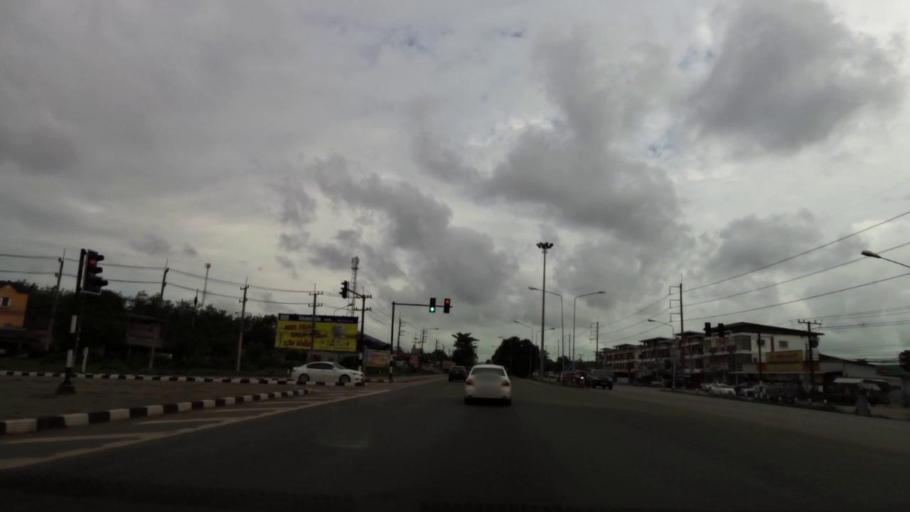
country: TH
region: Chanthaburi
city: Tha Mai
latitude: 12.7246
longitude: 101.9362
